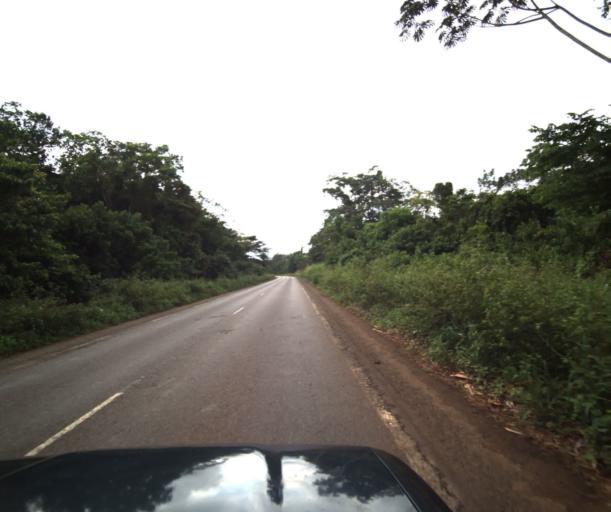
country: CM
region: Centre
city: Eseka
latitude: 3.8917
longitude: 10.7282
